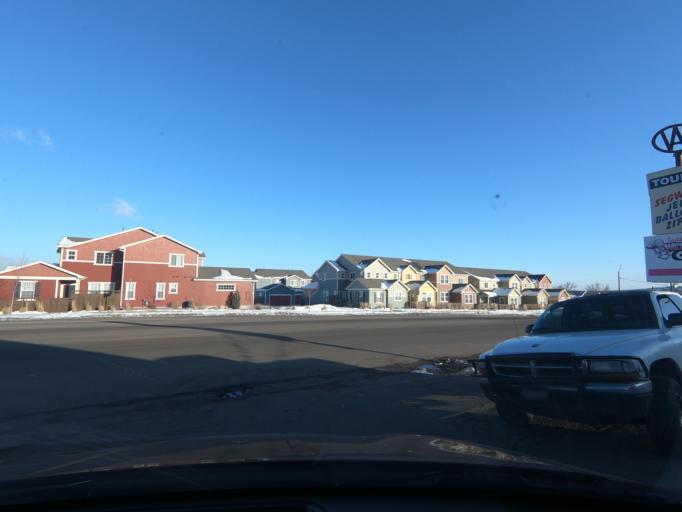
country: US
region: Colorado
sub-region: El Paso County
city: Colorado Springs
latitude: 38.8293
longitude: -104.8594
